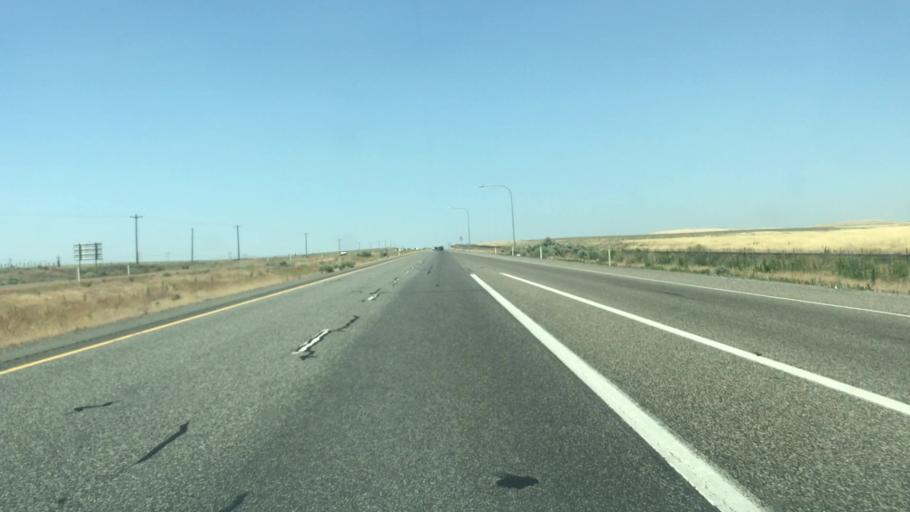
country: US
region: Washington
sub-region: Benton County
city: Highland
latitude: 46.0306
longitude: -119.2245
